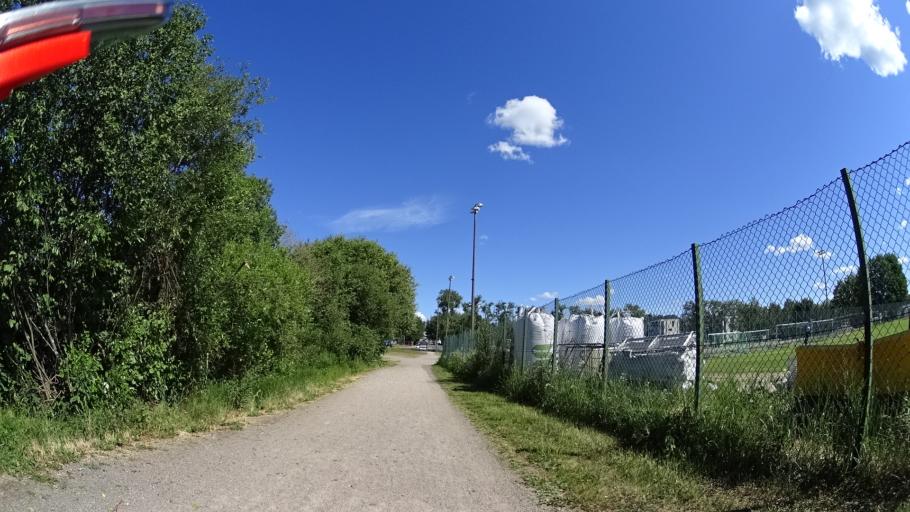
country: FI
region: Uusimaa
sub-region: Helsinki
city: Vantaa
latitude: 60.3005
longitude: 25.0216
